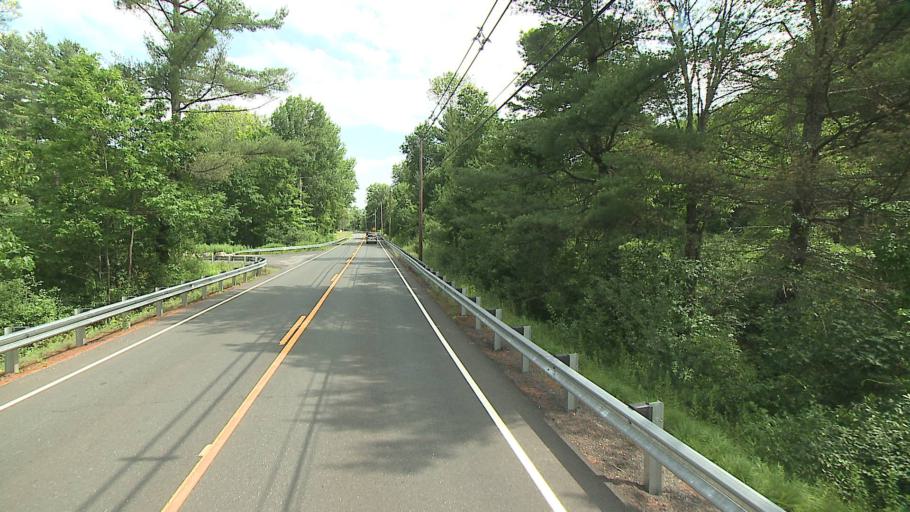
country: US
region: Connecticut
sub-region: Litchfield County
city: Winsted
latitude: 41.8842
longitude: -73.0750
